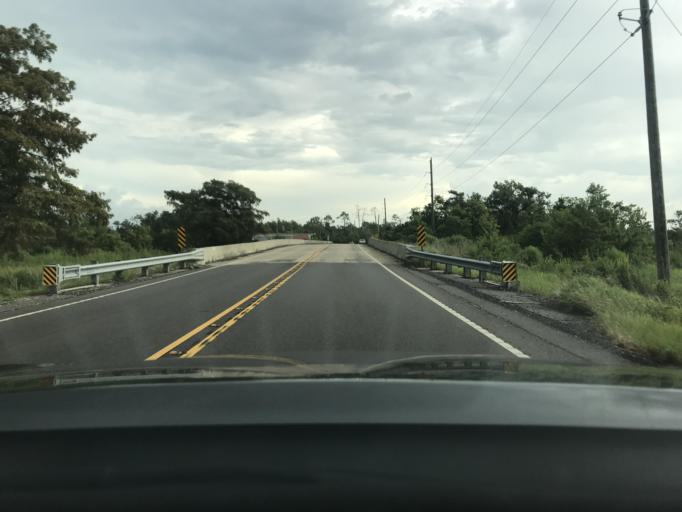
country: US
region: Louisiana
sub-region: Calcasieu Parish
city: Westlake
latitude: 30.2510
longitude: -93.2470
